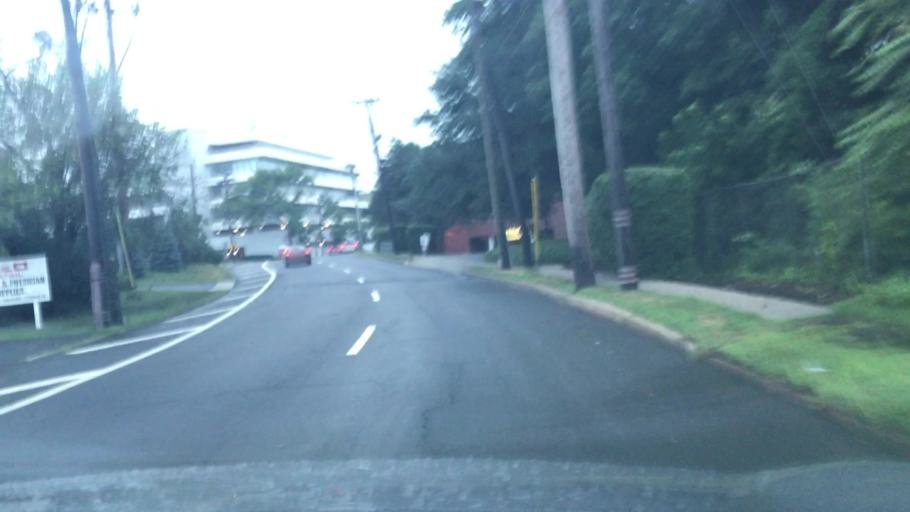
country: US
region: New Jersey
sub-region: Bergen County
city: Englewood
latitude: 40.9008
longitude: -73.9710
